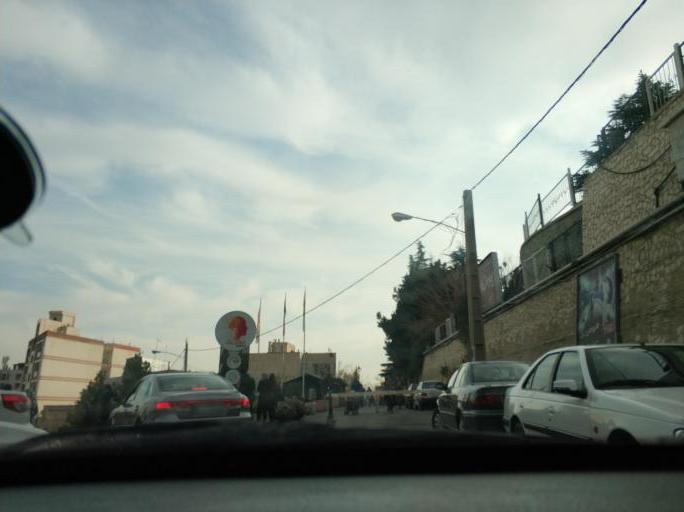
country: IR
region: Tehran
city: Tajrish
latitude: 35.8155
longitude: 51.4875
